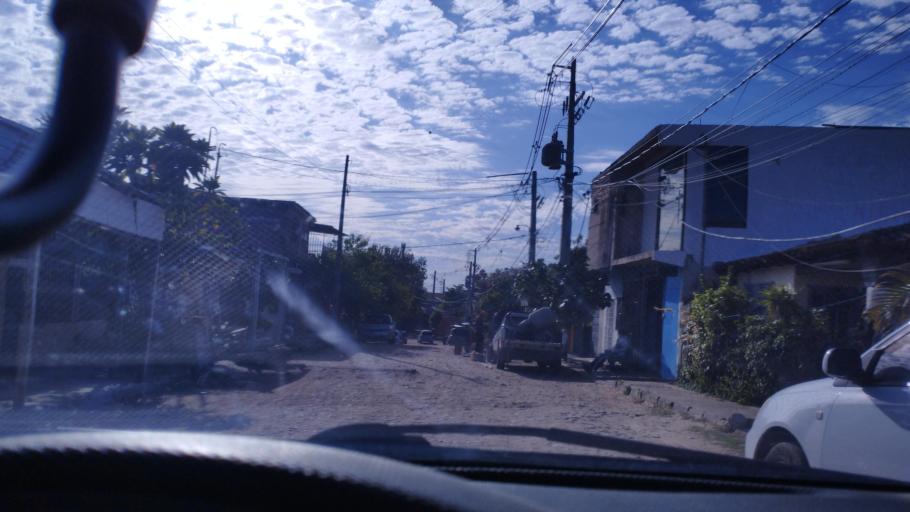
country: PY
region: Central
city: Colonia Mariano Roque Alonso
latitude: -25.2399
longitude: -57.5803
